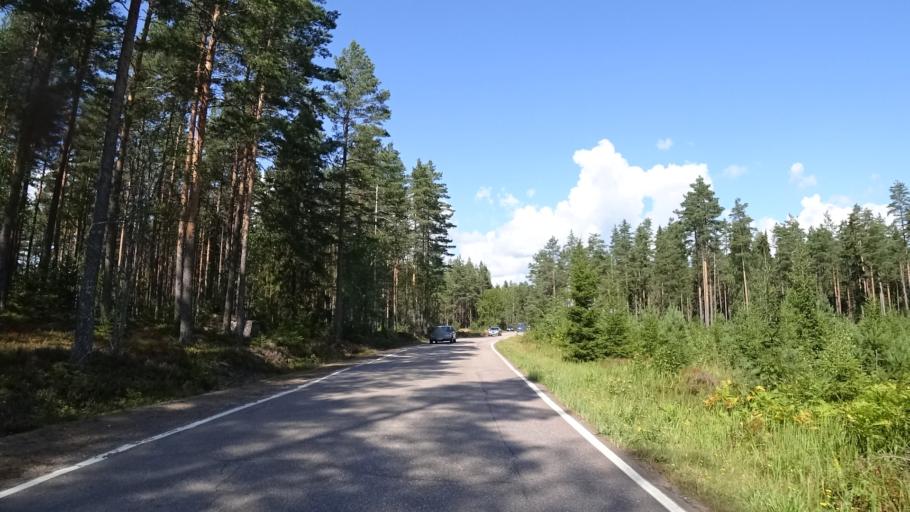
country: FI
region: Kymenlaakso
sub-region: Kotka-Hamina
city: Karhula
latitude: 60.5651
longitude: 26.9000
